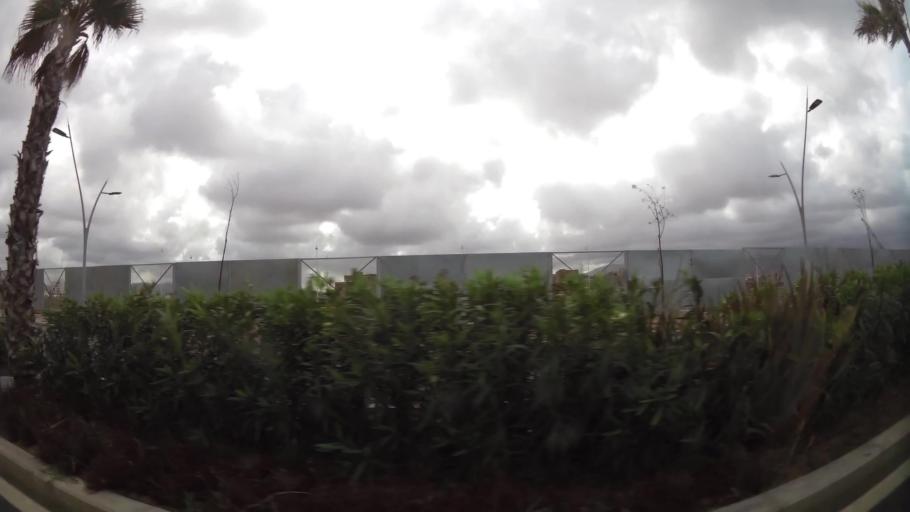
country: MA
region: Oriental
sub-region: Nador
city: Nador
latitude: 35.1589
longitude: -2.9065
